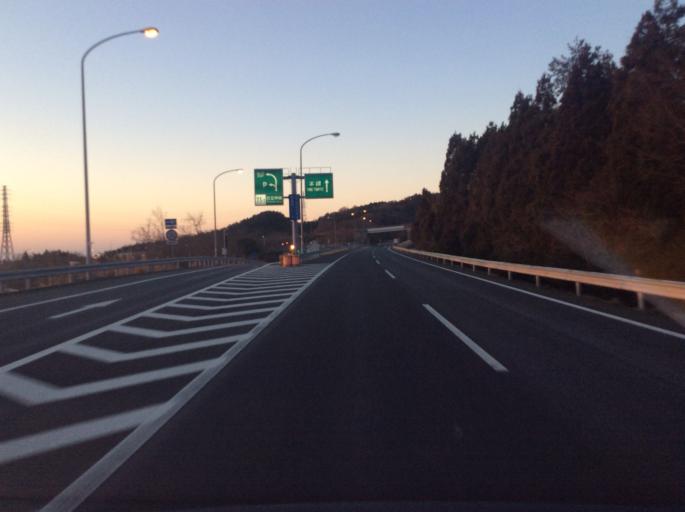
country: JP
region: Ibaraki
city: Hitachi
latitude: 36.6044
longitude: 140.6367
